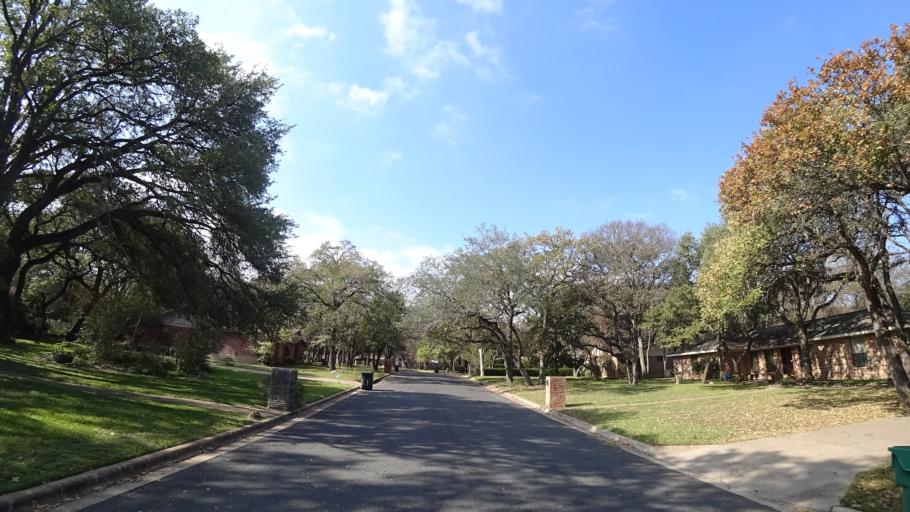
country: US
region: Texas
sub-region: Travis County
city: Shady Hollow
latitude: 30.1663
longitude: -97.8609
